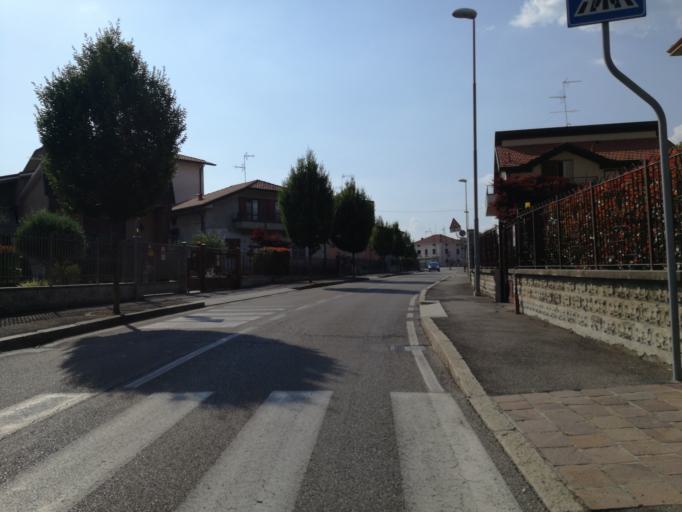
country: IT
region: Lombardy
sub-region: Provincia di Bergamo
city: Calusco d'Adda
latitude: 45.6907
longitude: 9.4696
